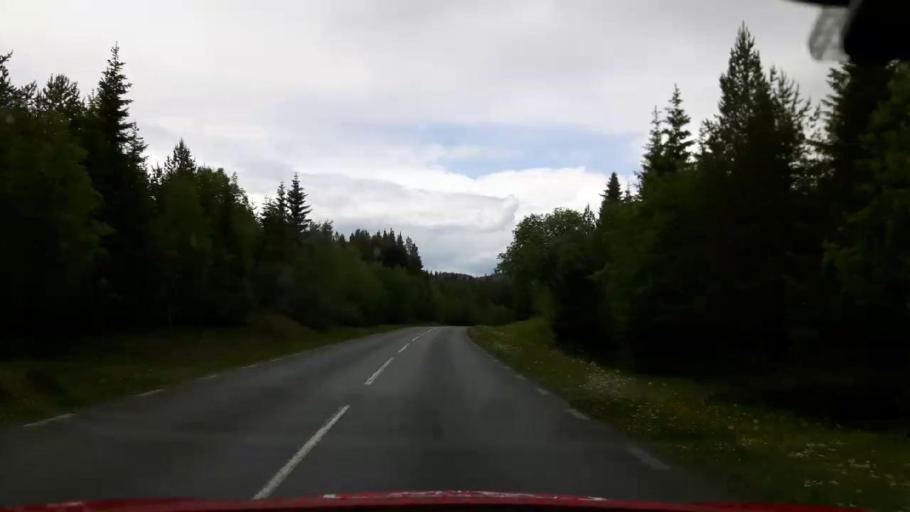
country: SE
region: Jaemtland
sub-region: Krokoms Kommun
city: Krokom
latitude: 63.4703
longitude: 14.1939
